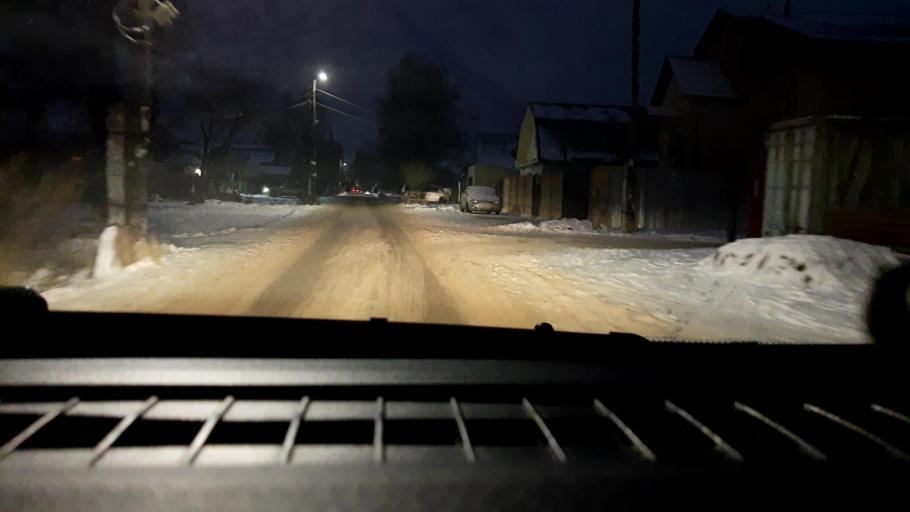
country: RU
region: Nizjnij Novgorod
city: Gorbatovka
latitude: 56.2549
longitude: 43.7470
